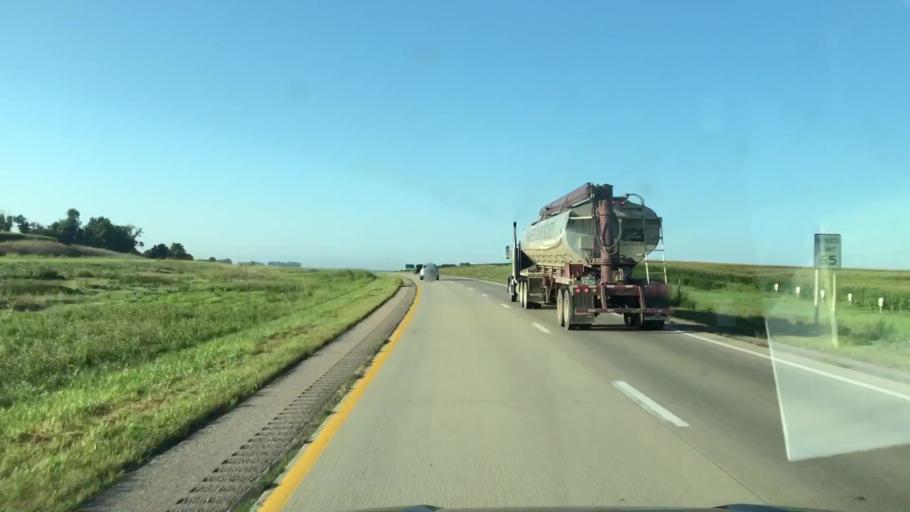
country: US
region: Iowa
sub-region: Sioux County
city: Alton
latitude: 43.0496
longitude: -95.9195
